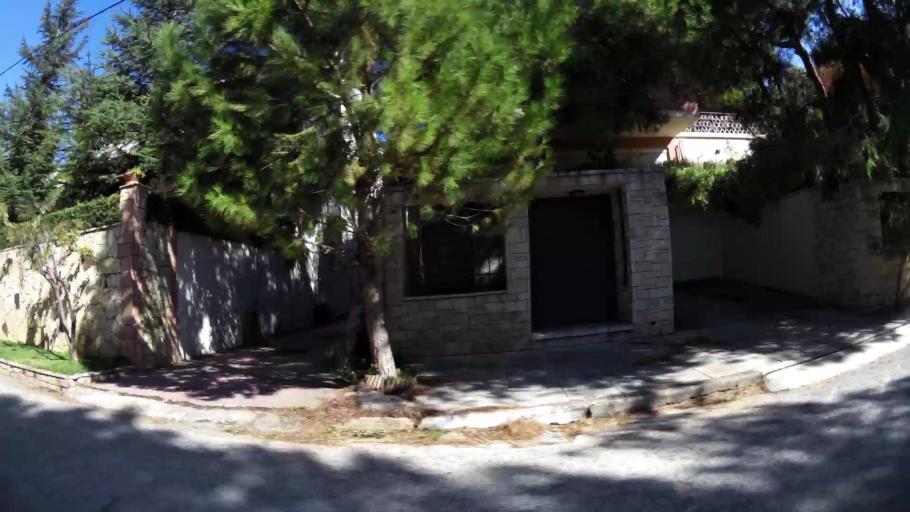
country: GR
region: Attica
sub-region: Nomarchia Anatolikis Attikis
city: Dioni
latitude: 38.0268
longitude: 23.9341
